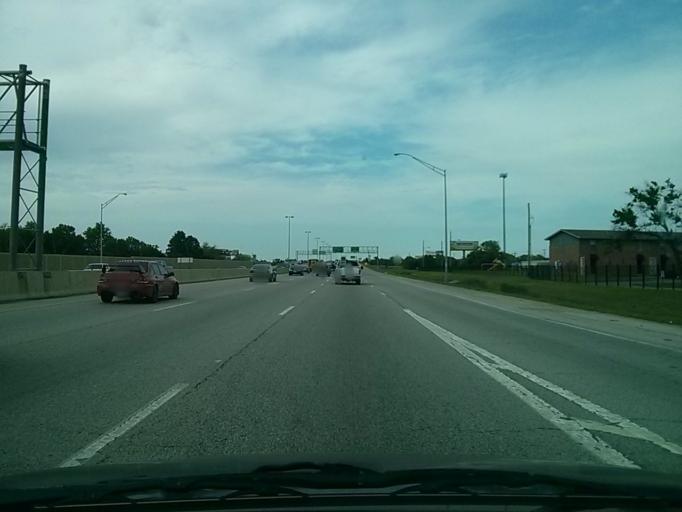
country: US
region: Oklahoma
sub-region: Tulsa County
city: Broken Arrow
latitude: 36.1424
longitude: -95.8601
